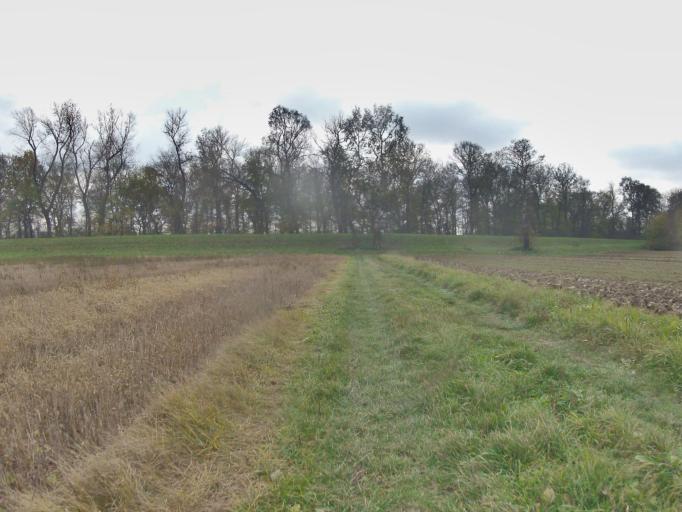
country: PL
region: Lesser Poland Voivodeship
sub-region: Powiat wielicki
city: Wegrzce Wielkie
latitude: 50.0463
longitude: 20.1085
